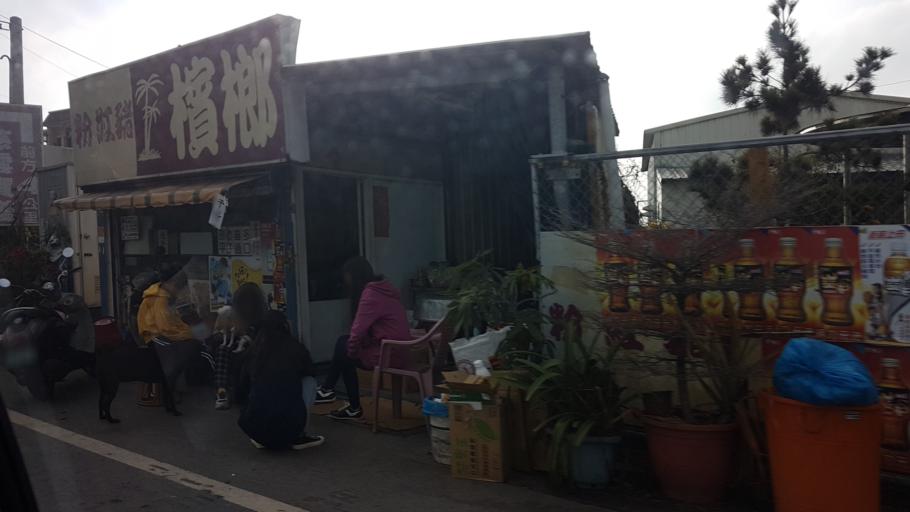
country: TW
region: Taiwan
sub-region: Chiayi
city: Jiayi Shi
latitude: 23.4210
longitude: 120.4308
